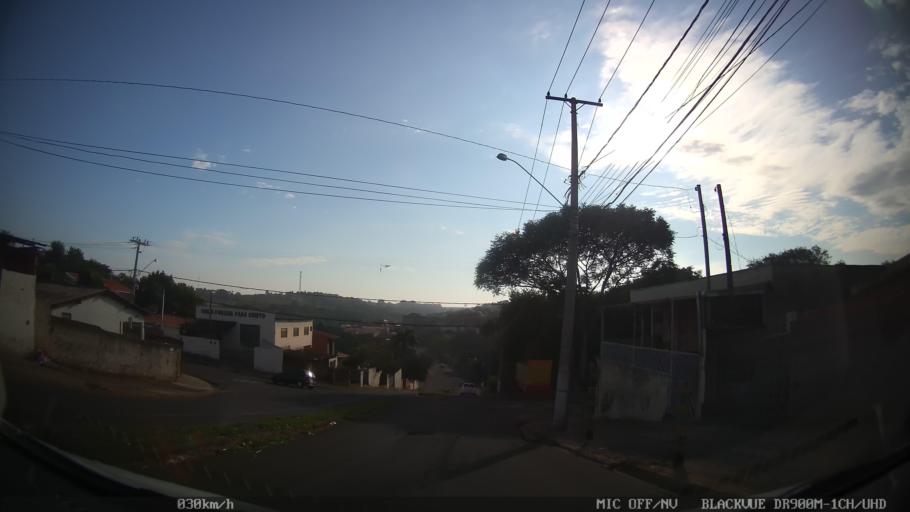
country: BR
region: Sao Paulo
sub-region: Santa Barbara D'Oeste
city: Santa Barbara d'Oeste
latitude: -22.7305
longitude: -47.3780
